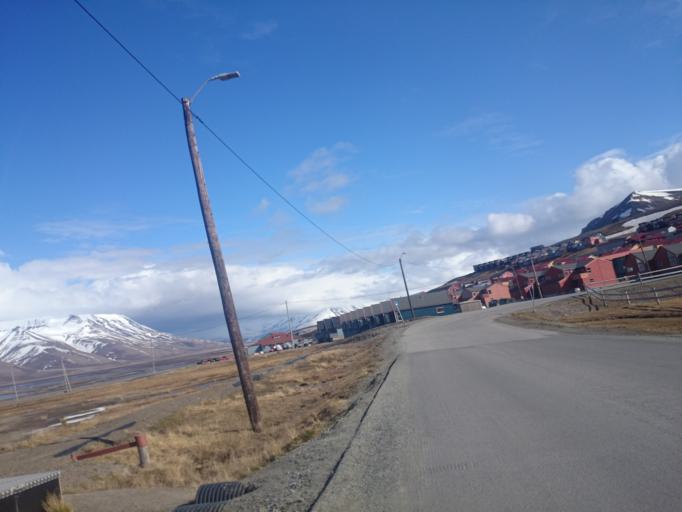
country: SJ
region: Svalbard
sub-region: Spitsbergen
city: Longyearbyen
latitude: 78.2219
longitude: 15.6525
